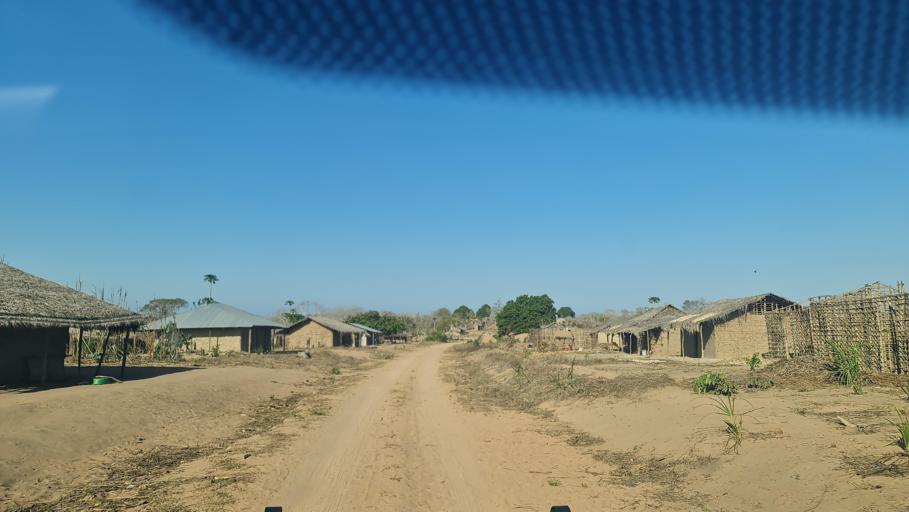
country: MZ
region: Nampula
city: Nacala
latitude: -13.9412
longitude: 40.4856
